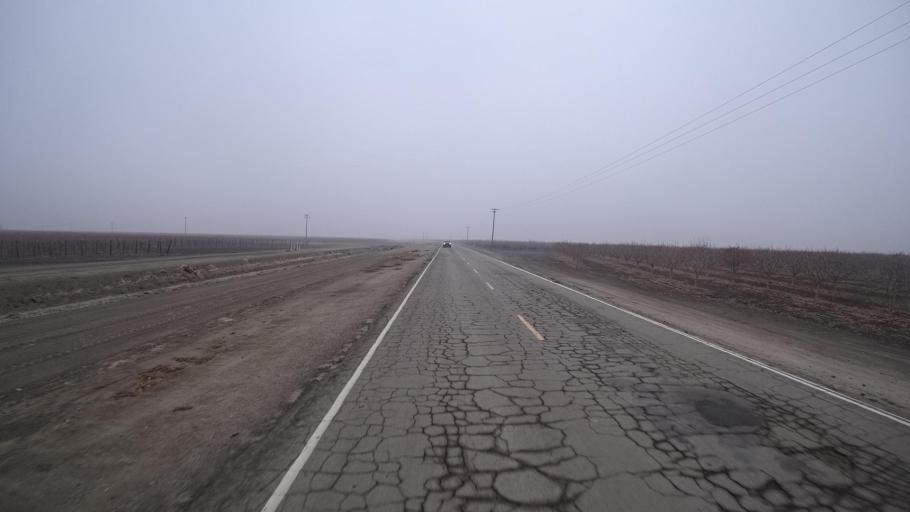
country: US
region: California
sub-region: Kern County
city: Lost Hills
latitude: 35.5149
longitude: -119.6157
